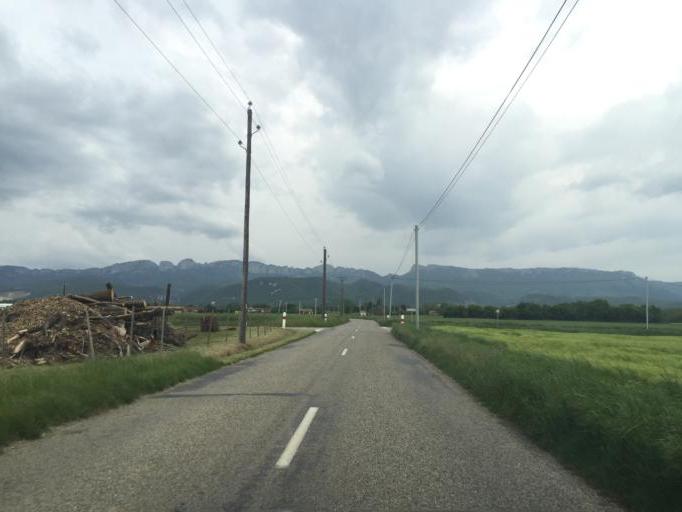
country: FR
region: Rhone-Alpes
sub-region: Departement de la Drome
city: Chatuzange-le-Goubet
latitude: 44.9626
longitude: 5.0899
